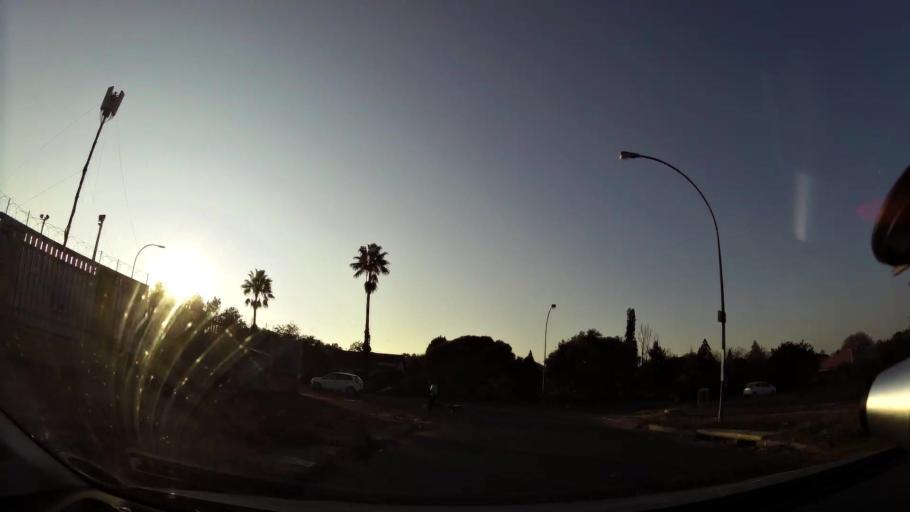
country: ZA
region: Orange Free State
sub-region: Mangaung Metropolitan Municipality
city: Bloemfontein
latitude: -29.0972
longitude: 26.1603
